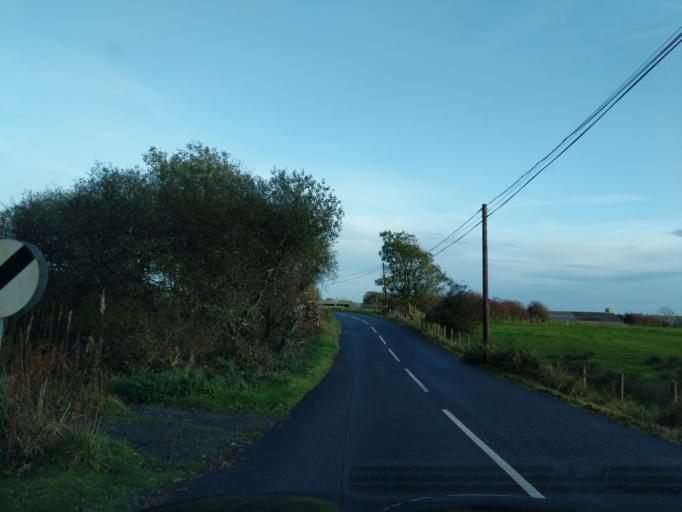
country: GB
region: Scotland
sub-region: Dumfries and Galloway
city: Kirkcudbright
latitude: 54.8111
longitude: -4.1331
